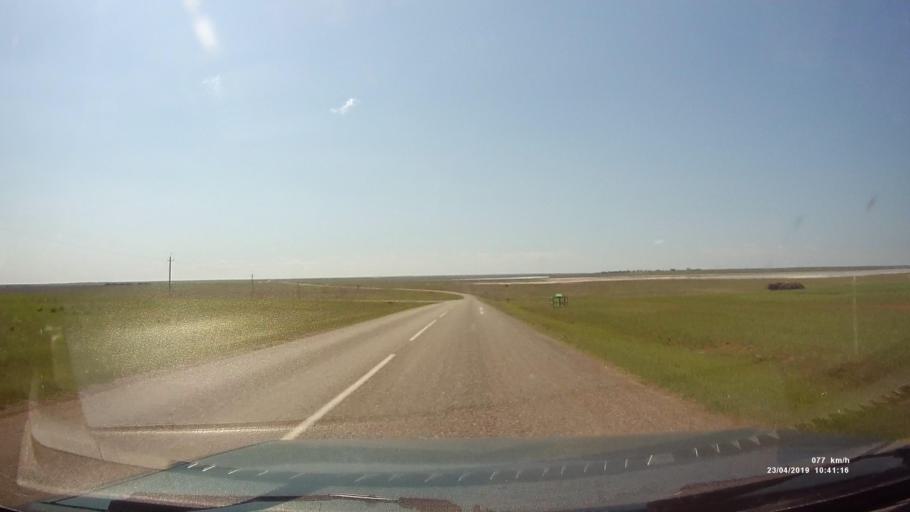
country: RU
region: Kalmykiya
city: Yashalta
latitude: 46.4958
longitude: 42.6382
